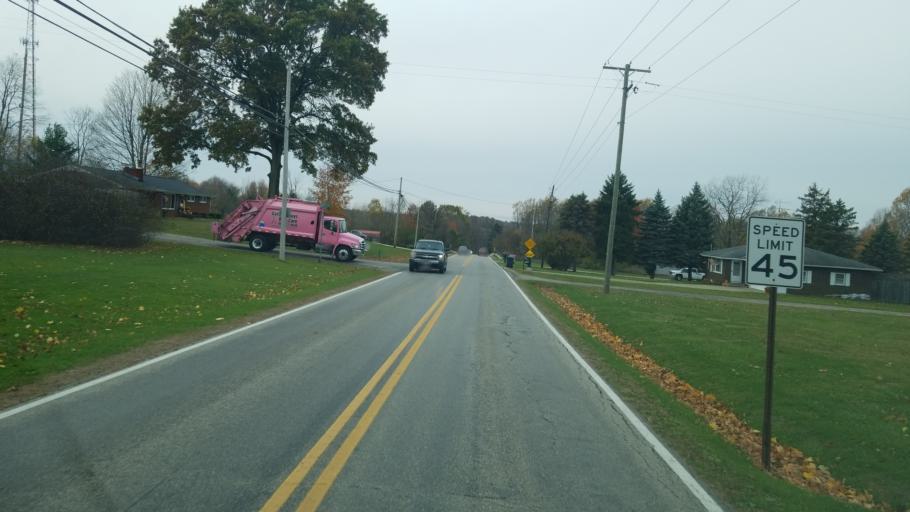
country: US
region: Ohio
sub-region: Richland County
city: Lincoln Heights
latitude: 40.7239
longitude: -82.4751
